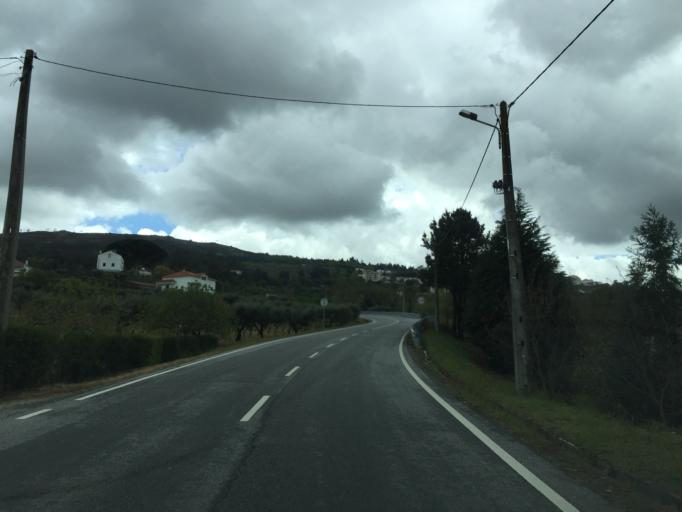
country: PT
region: Guarda
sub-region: Manteigas
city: Manteigas
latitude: 40.5072
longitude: -7.5884
